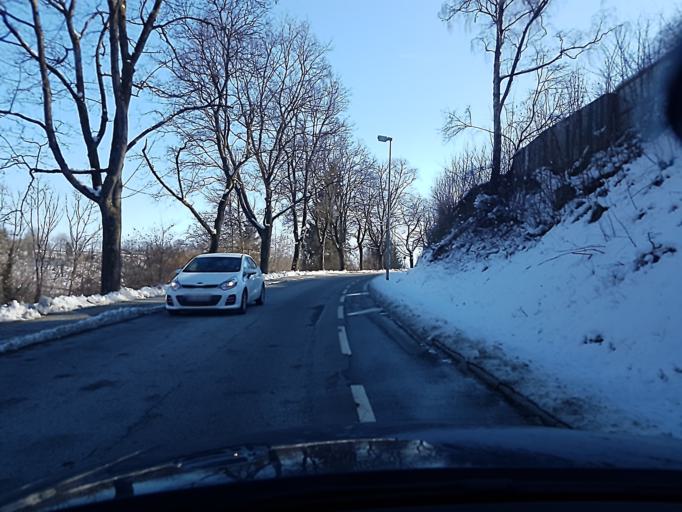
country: DE
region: Baden-Wuerttemberg
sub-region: Freiburg Region
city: Rottweil
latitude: 48.1758
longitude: 8.6258
